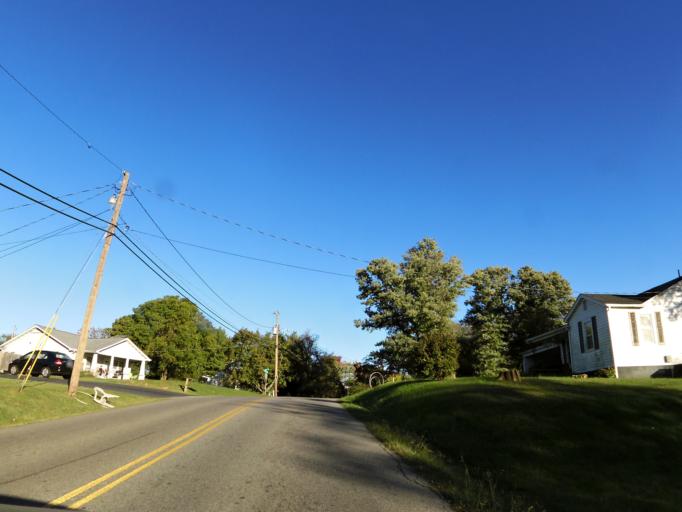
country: US
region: Tennessee
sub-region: Blount County
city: Eagleton Village
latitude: 35.7760
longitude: -83.9489
